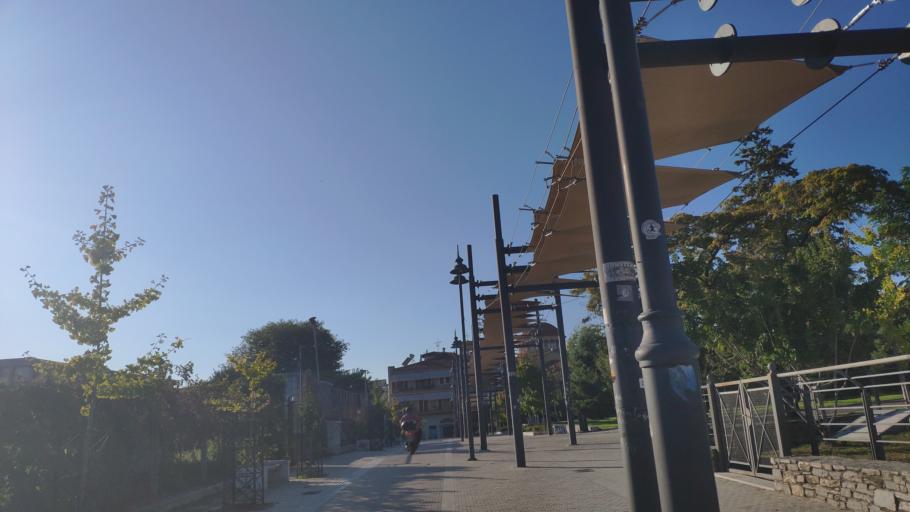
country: GR
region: Thessaly
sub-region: Nomos Larisis
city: Larisa
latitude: 39.6409
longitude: 22.4156
